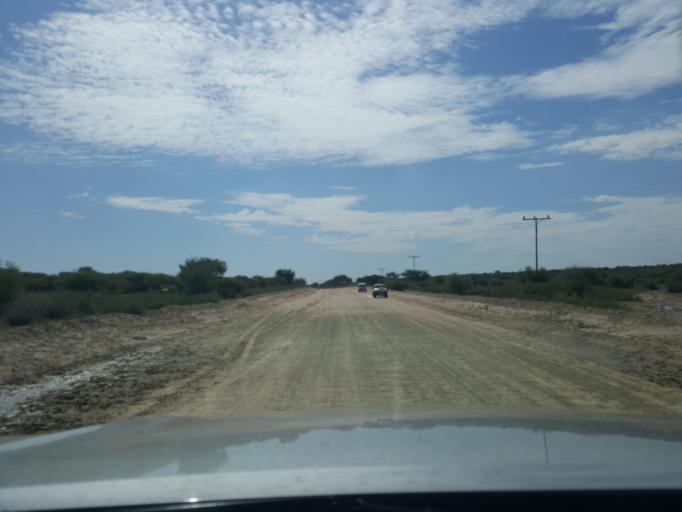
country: BW
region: Kweneng
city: Letlhakeng
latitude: -24.0496
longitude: 25.0229
